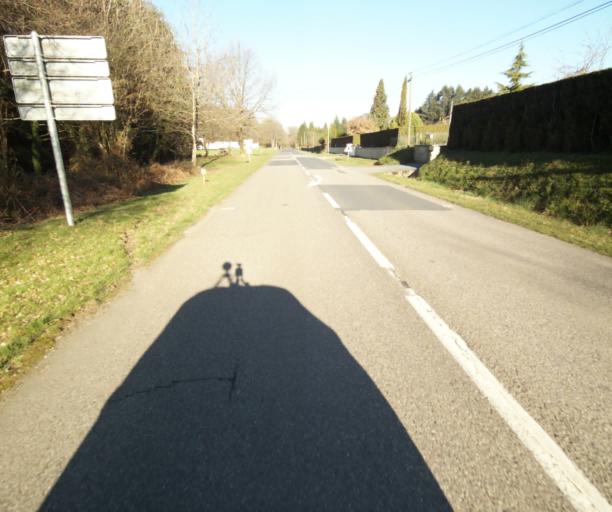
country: FR
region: Limousin
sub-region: Departement de la Correze
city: Uzerche
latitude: 45.3873
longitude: 1.6032
